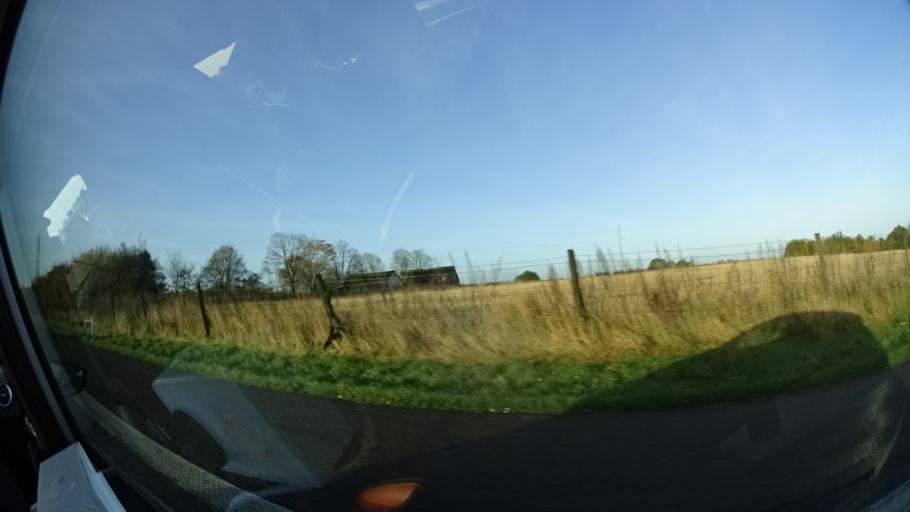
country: DK
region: Central Jutland
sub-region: Horsens Kommune
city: Horsens
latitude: 55.9395
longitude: 9.8189
